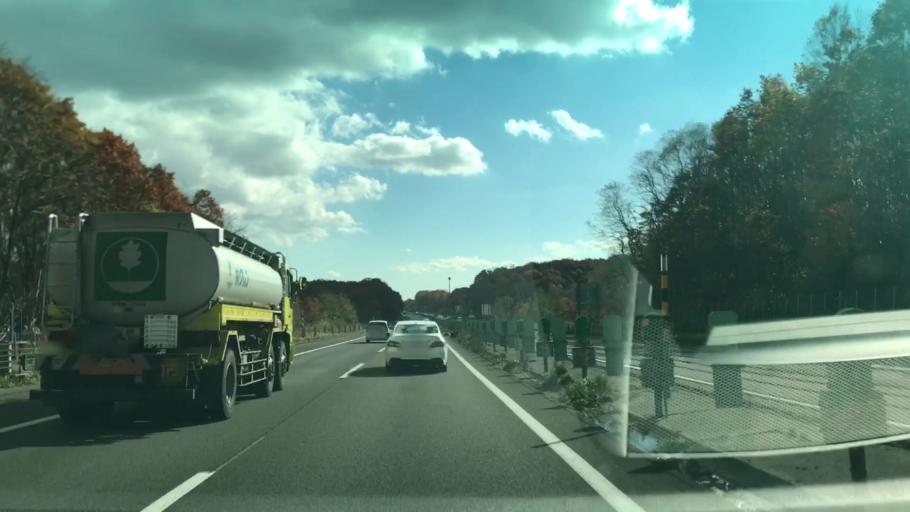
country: JP
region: Hokkaido
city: Kitahiroshima
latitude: 42.9453
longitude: 141.5179
